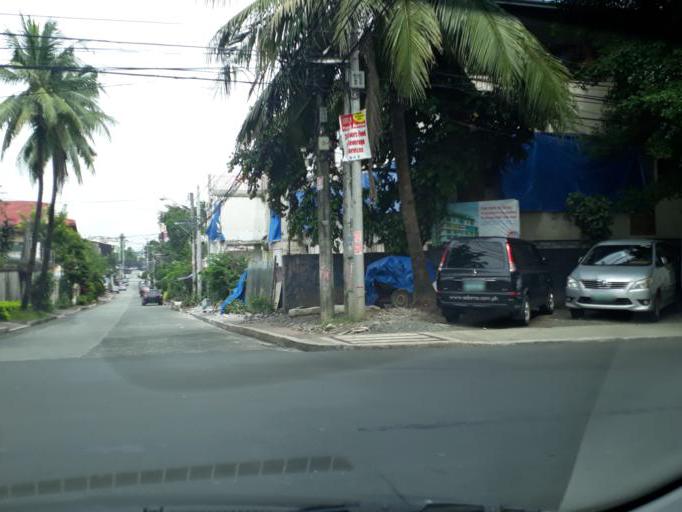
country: PH
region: Metro Manila
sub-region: Quezon City
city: Quezon City
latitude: 14.6322
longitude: 121.0371
